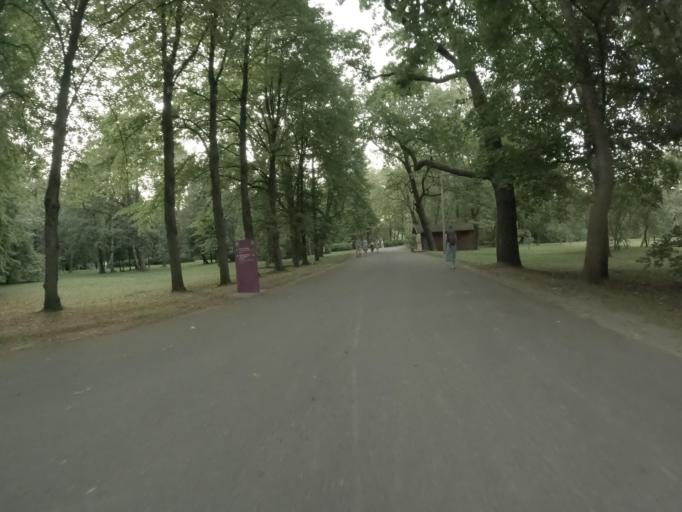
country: RU
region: Leningrad
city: Krestovskiy ostrov
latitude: 59.9794
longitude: 30.2536
